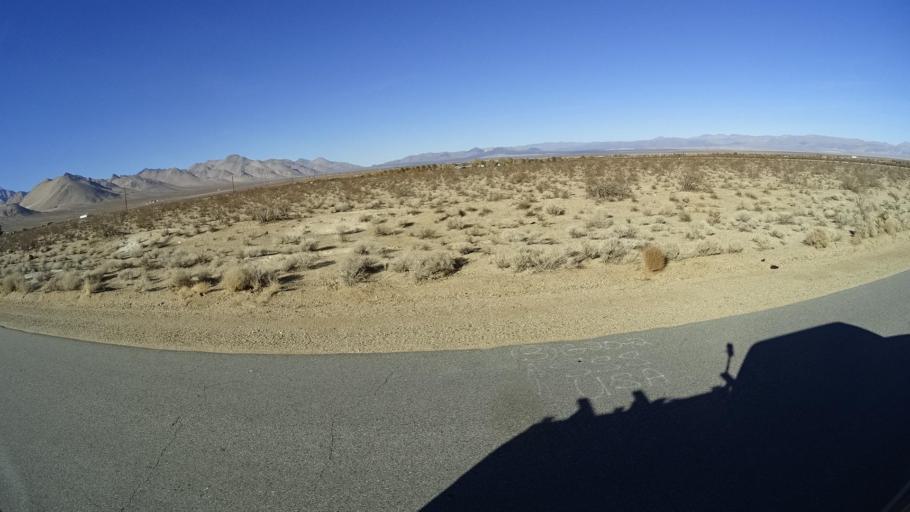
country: US
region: California
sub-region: Kern County
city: Inyokern
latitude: 35.6793
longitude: -117.8432
